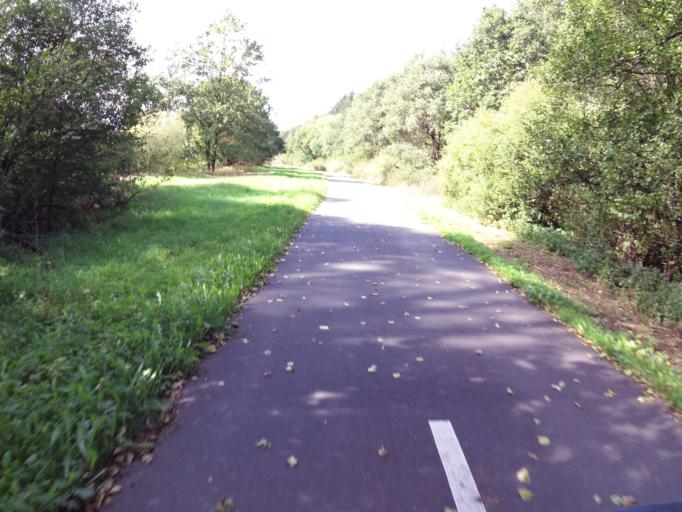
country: DE
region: Rheinland-Pfalz
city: Pronsfeld
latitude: 50.1857
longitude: 6.3088
